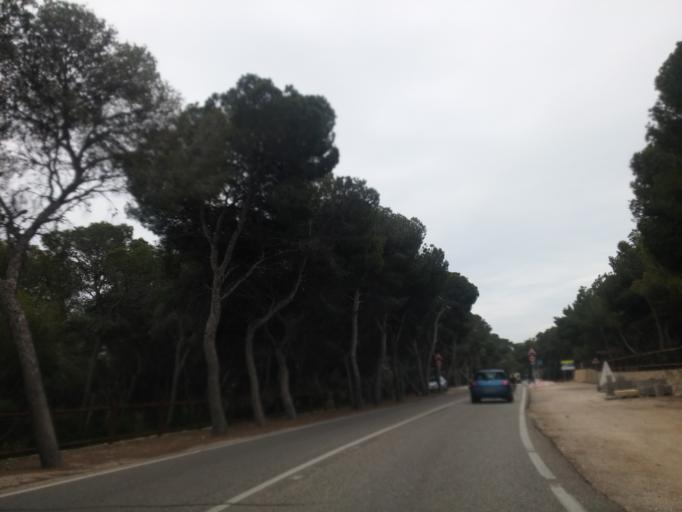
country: ES
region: Valencia
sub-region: Provincia de Alicante
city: Moraira
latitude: 38.6710
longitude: 0.0920
